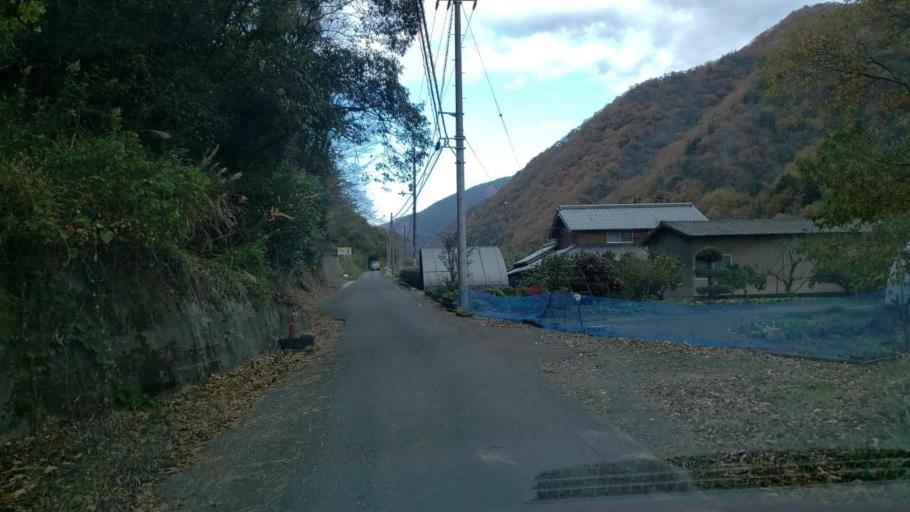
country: JP
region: Tokushima
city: Wakimachi
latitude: 34.1153
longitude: 134.2252
